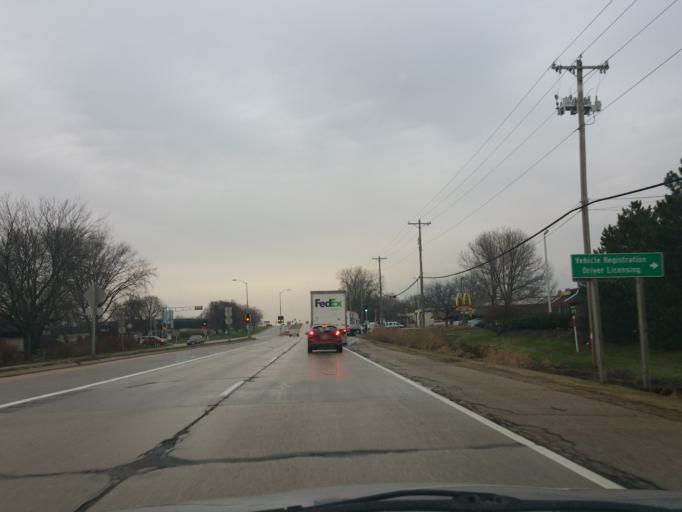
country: US
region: Wisconsin
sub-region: Dane County
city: Maple Bluff
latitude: 43.1246
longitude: -89.3250
